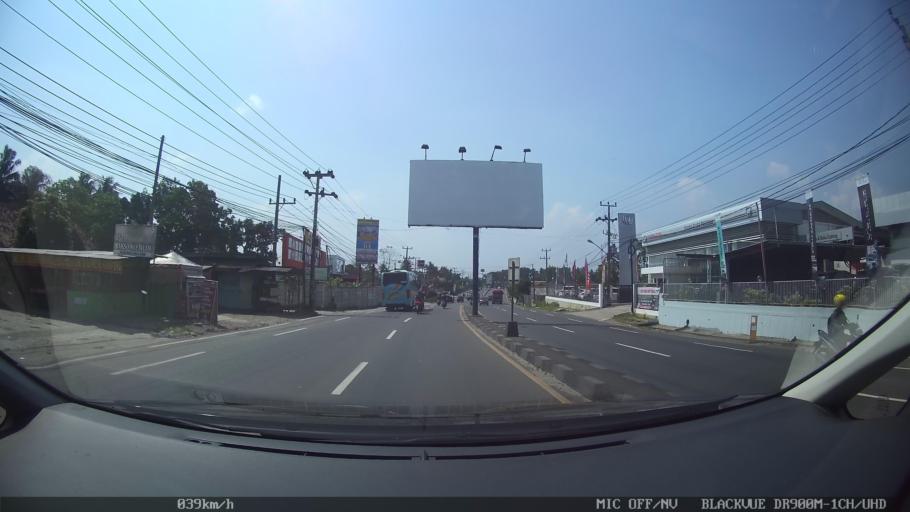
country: ID
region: Lampung
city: Natar
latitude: -5.3520
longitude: 105.2182
